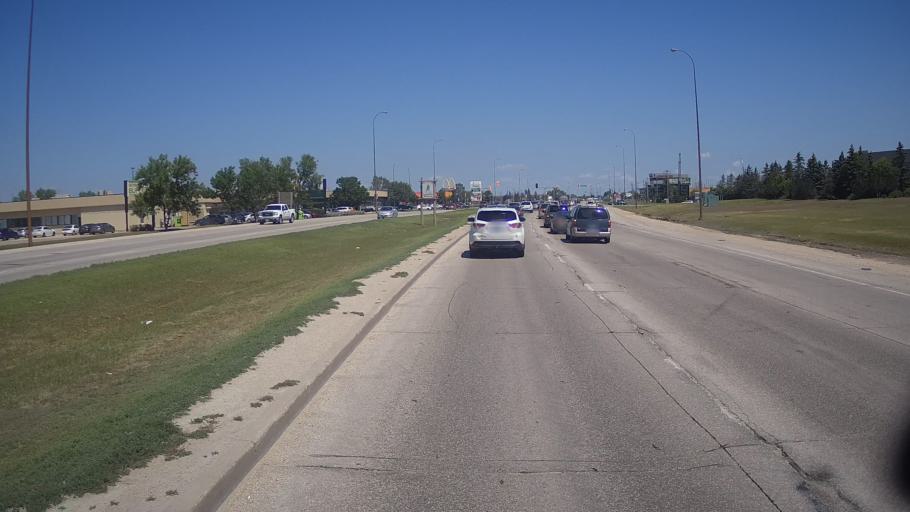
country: CA
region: Manitoba
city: Winnipeg
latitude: 49.9005
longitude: -97.0679
